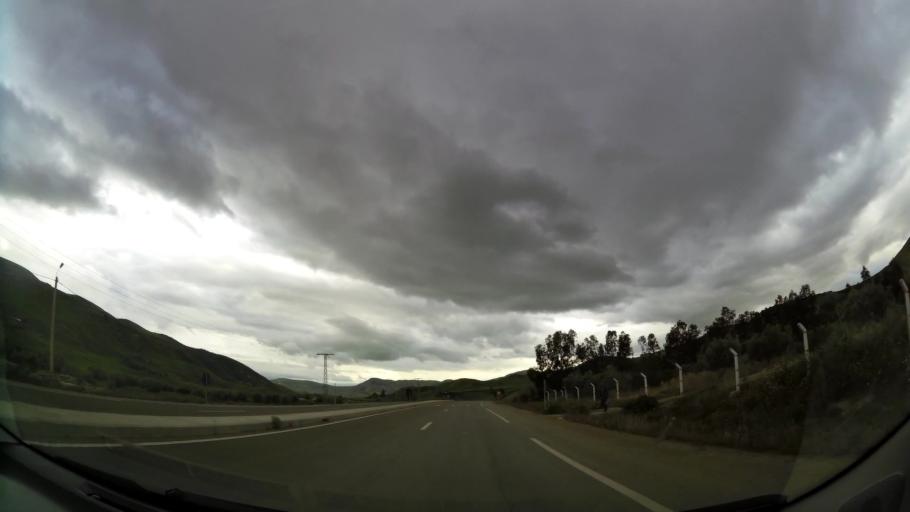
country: MA
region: Taza-Al Hoceima-Taounate
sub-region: Taza
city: Taza
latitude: 34.3388
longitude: -3.9381
